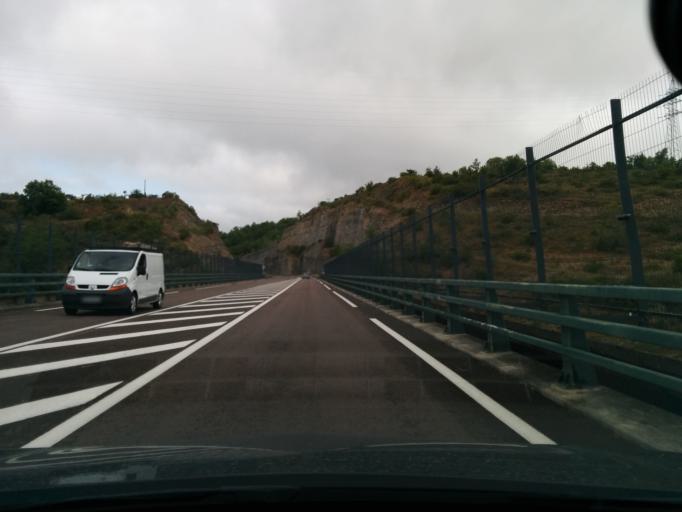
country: FR
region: Midi-Pyrenees
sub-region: Departement du Lot
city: Cahors
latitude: 44.4441
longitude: 1.4226
